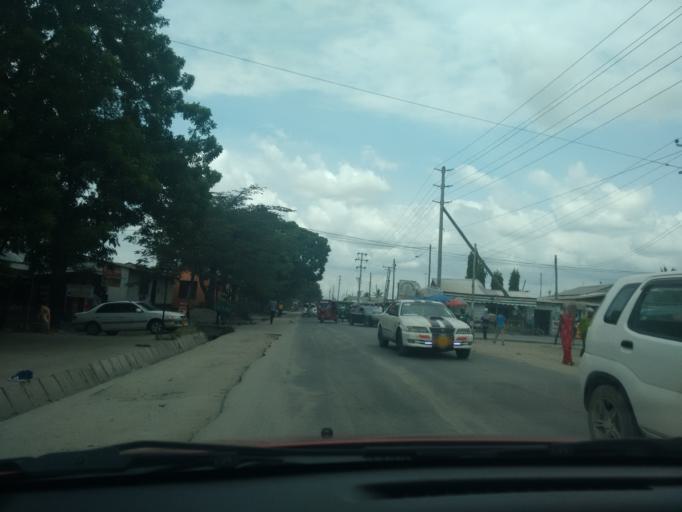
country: TZ
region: Dar es Salaam
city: Dar es Salaam
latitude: -6.8525
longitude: 39.2527
